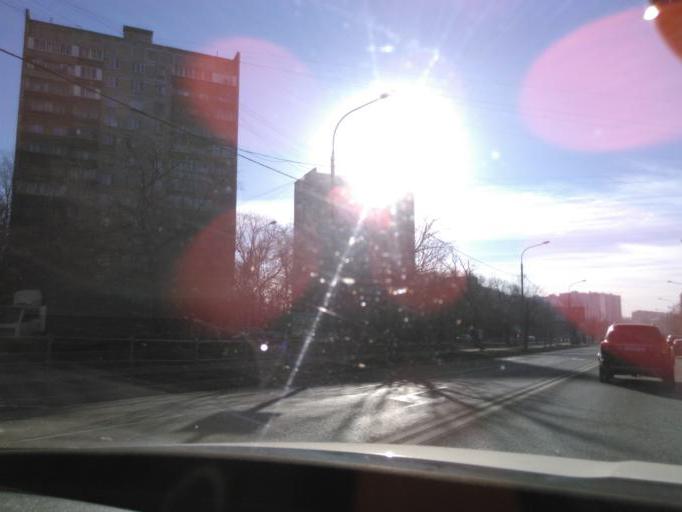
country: RU
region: Moscow
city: Novokhovrino
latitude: 55.8574
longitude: 37.5116
